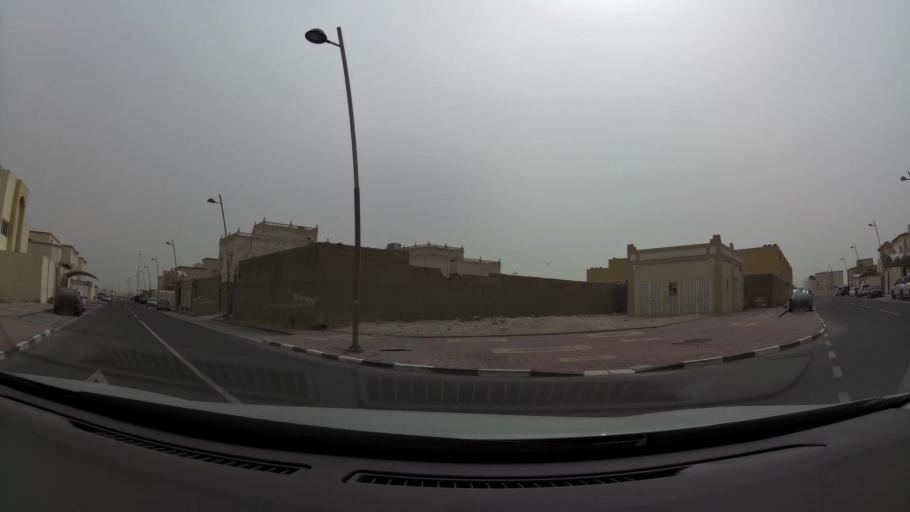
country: QA
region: Baladiyat ad Dawhah
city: Doha
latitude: 25.2290
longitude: 51.5536
